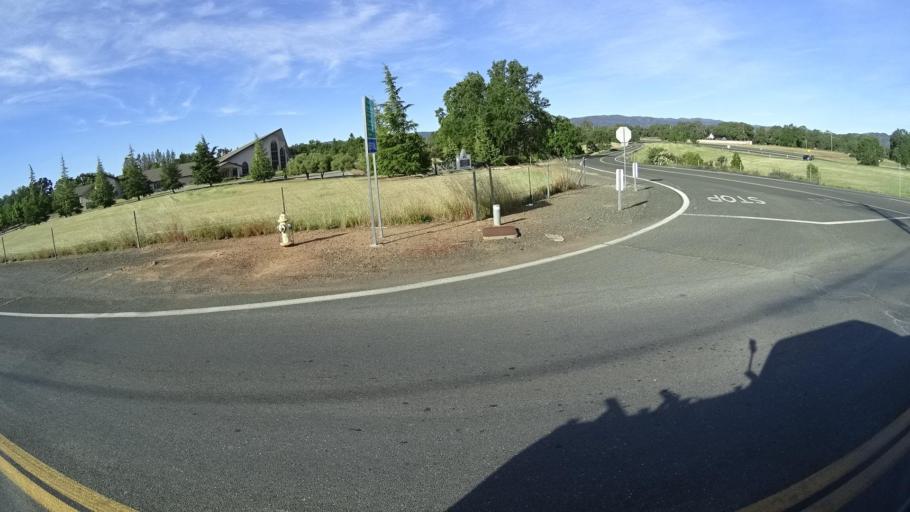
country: US
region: California
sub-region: Lake County
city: North Lakeport
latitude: 39.0833
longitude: -122.9249
